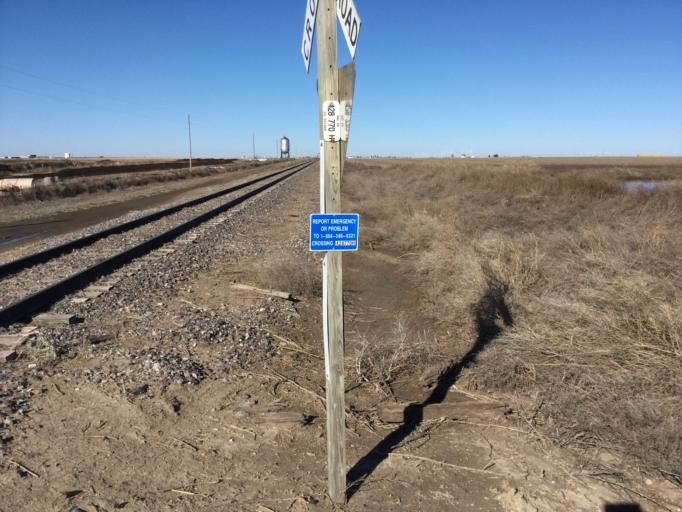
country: US
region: Kansas
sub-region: Scott County
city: Scott City
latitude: 38.4869
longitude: -101.0358
